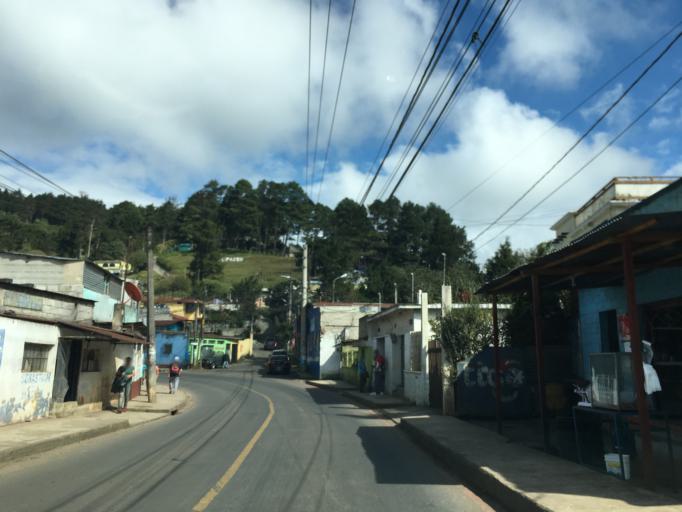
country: GT
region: Guatemala
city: San Jose Pinula
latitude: 14.5477
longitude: -90.4389
